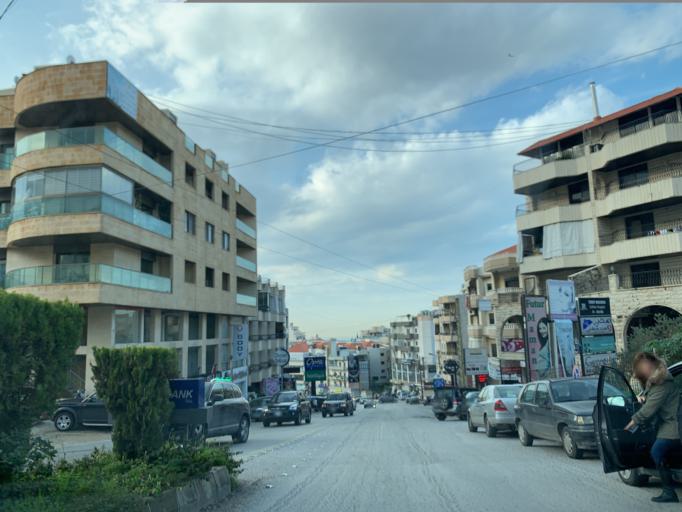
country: LB
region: Mont-Liban
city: Jdaidet el Matn
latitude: 33.8553
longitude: 35.5760
